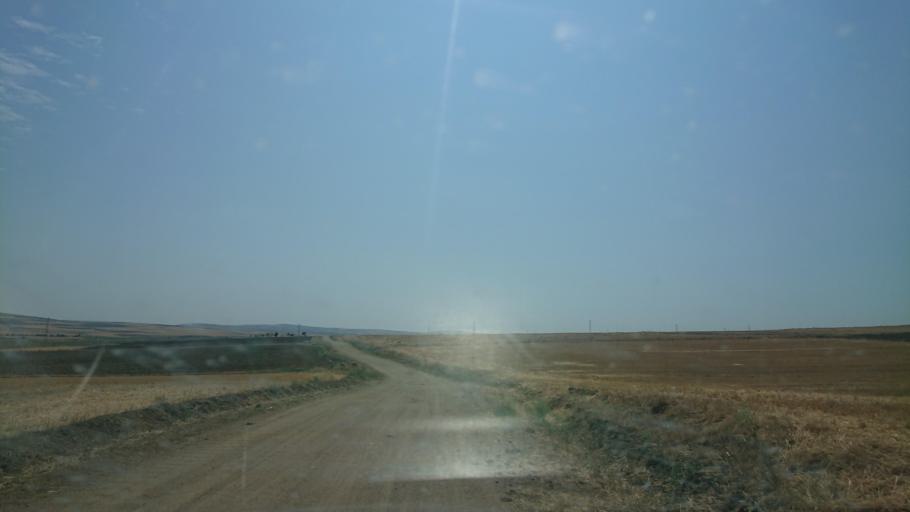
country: TR
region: Aksaray
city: Sariyahsi
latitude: 38.9571
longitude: 33.9007
